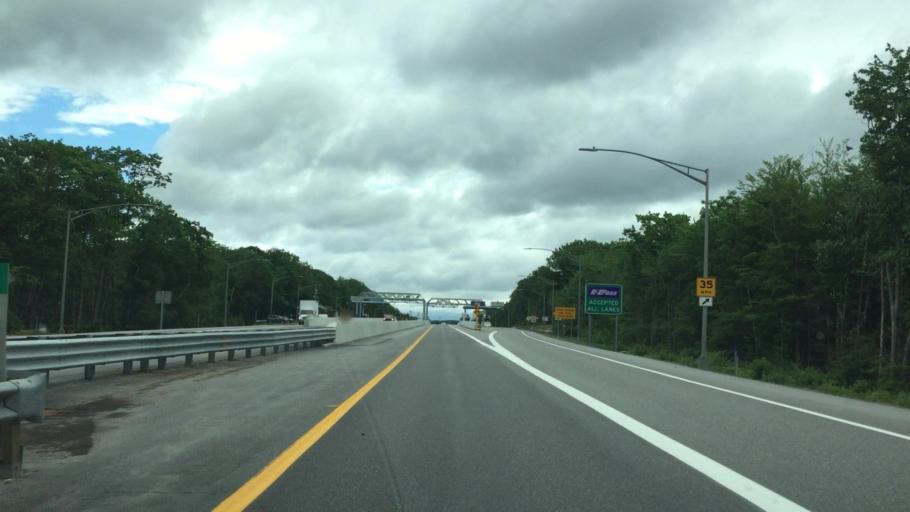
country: US
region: Maine
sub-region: Cumberland County
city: Falmouth
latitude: 43.7328
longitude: -70.2576
